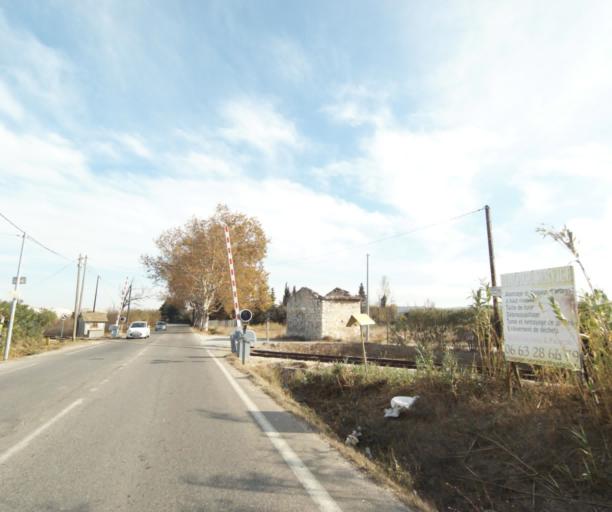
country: FR
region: Provence-Alpes-Cote d'Azur
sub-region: Departement des Bouches-du-Rhone
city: Chateauneuf-les-Martigues
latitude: 43.3929
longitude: 5.1861
